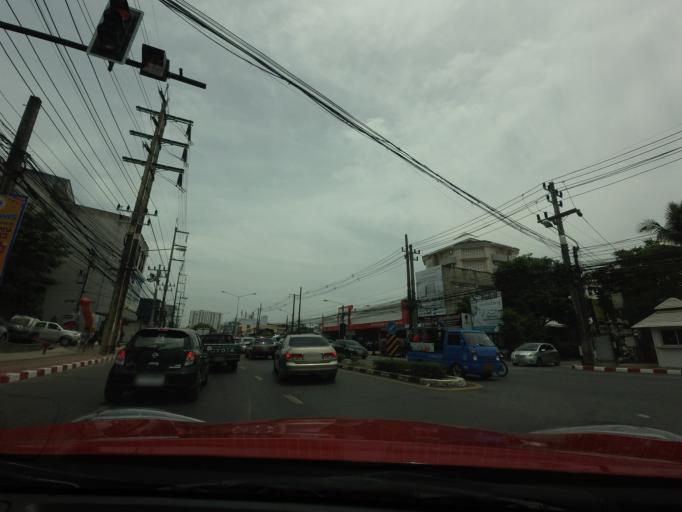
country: TH
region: Songkhla
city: Hat Yai
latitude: 7.0014
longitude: 100.4907
